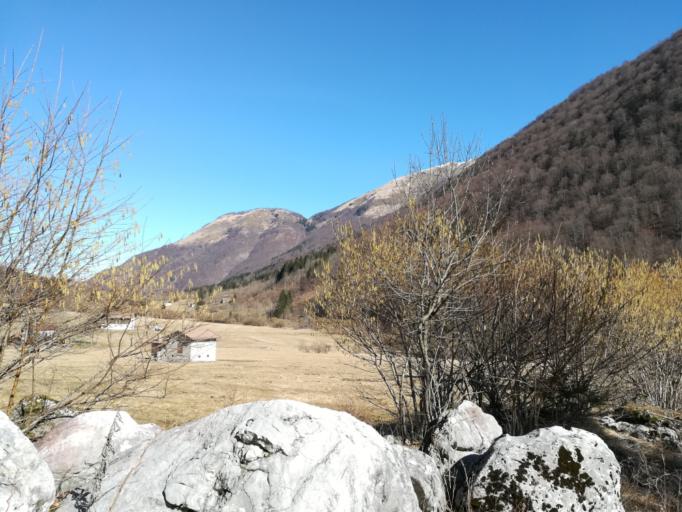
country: IT
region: Friuli Venezia Giulia
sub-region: Provincia di Udine
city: Preone
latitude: 46.3434
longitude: 12.8801
